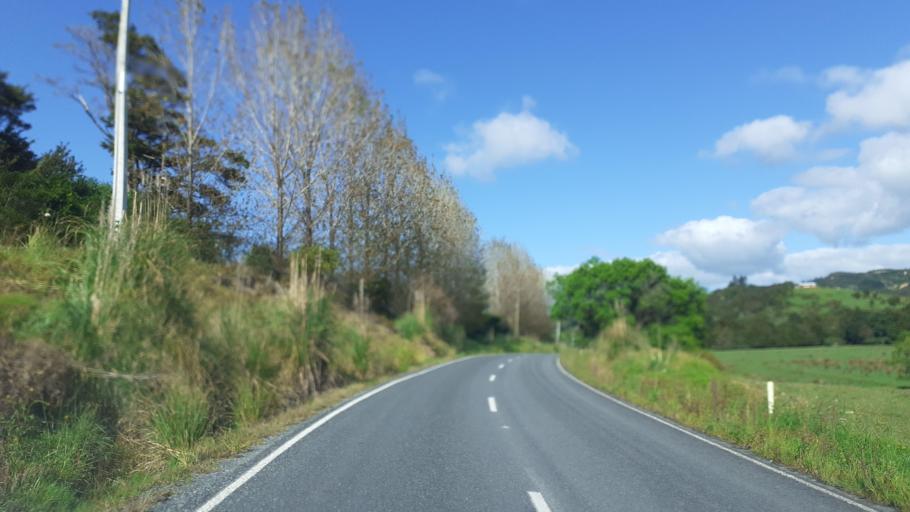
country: NZ
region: Northland
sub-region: Far North District
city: Moerewa
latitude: -35.4316
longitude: 173.9785
